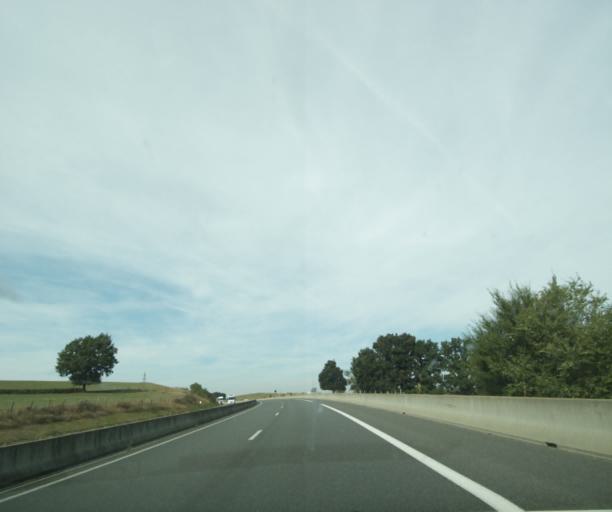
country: FR
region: Auvergne
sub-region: Departement de l'Allier
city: Lapalisse
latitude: 46.2352
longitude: 3.6425
